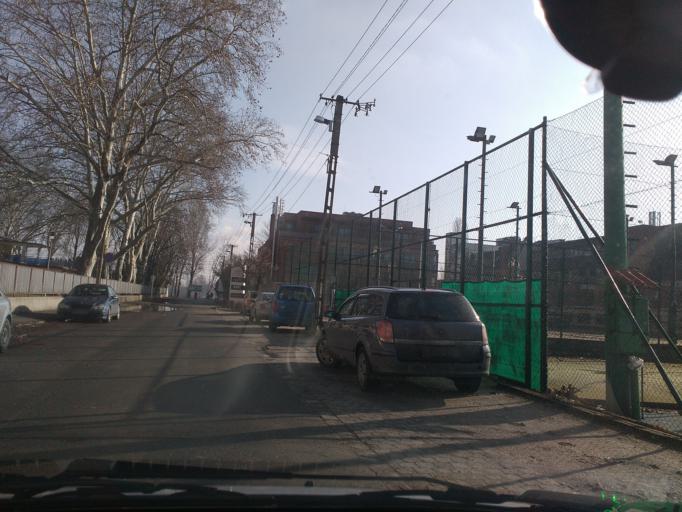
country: HU
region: Pest
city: Budakalasz
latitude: 47.5880
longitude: 19.0668
